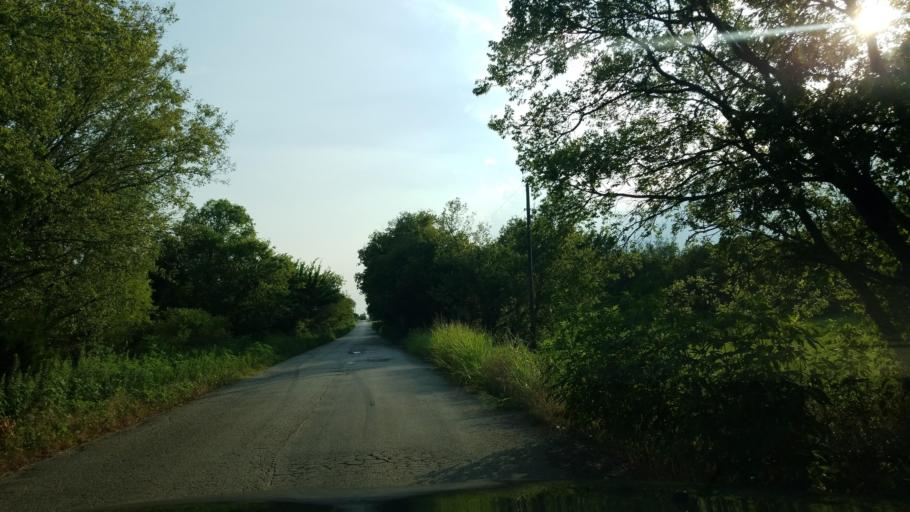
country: US
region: Texas
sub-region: Denton County
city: Denton
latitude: 33.2433
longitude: -97.0708
